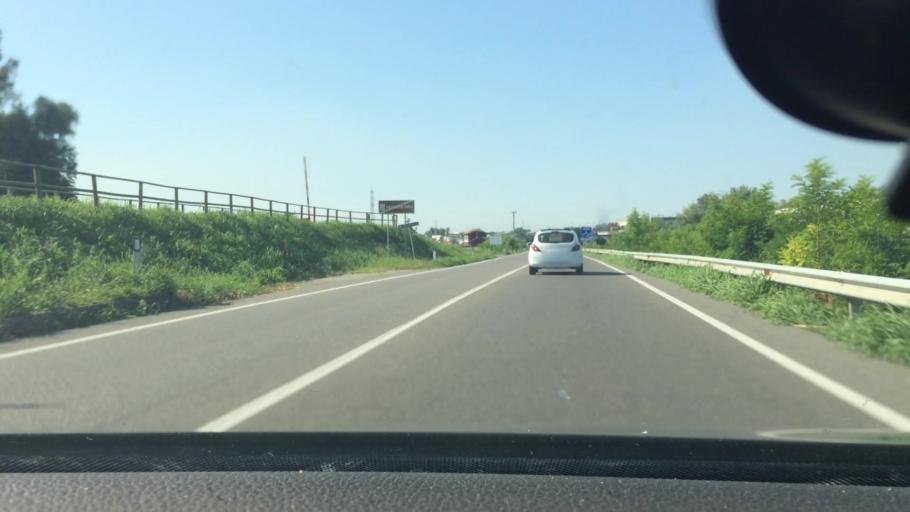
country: IT
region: Lombardy
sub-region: Provincia di Lodi
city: San Rocco al Porto
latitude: 45.0933
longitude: 9.6894
